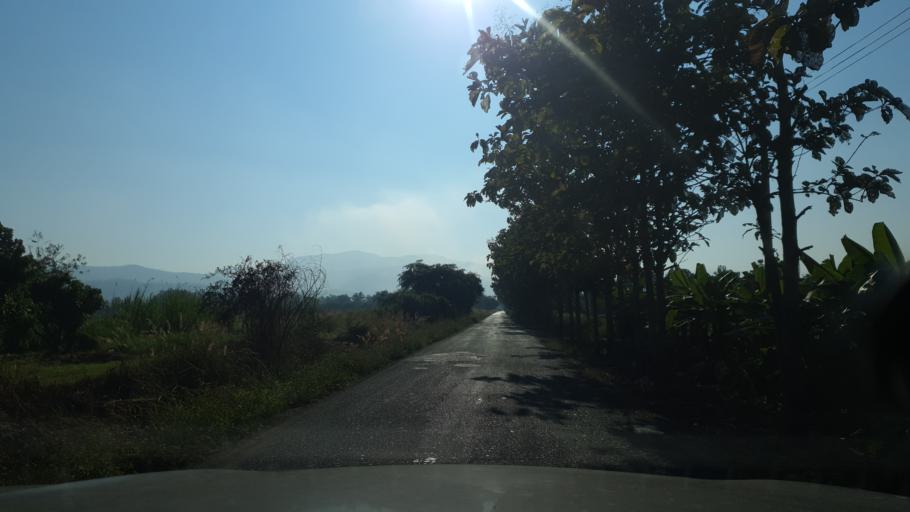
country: TH
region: Chiang Mai
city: San Kamphaeng
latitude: 18.6974
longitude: 99.1482
